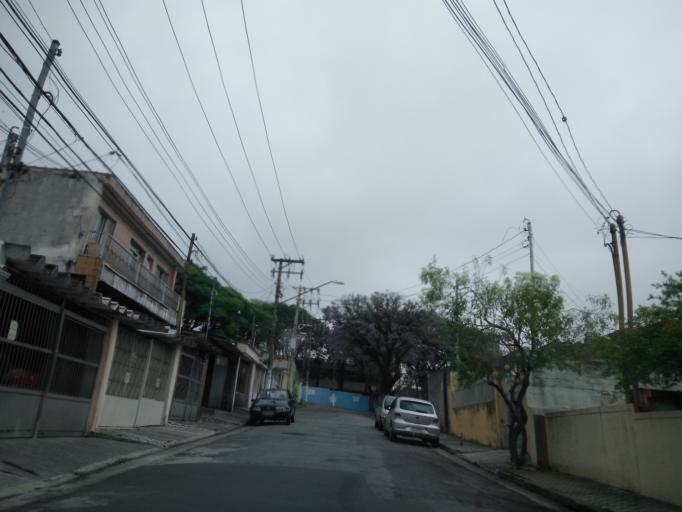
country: BR
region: Sao Paulo
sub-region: Sao Bernardo Do Campo
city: Sao Bernardo do Campo
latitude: -23.6938
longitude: -46.5709
